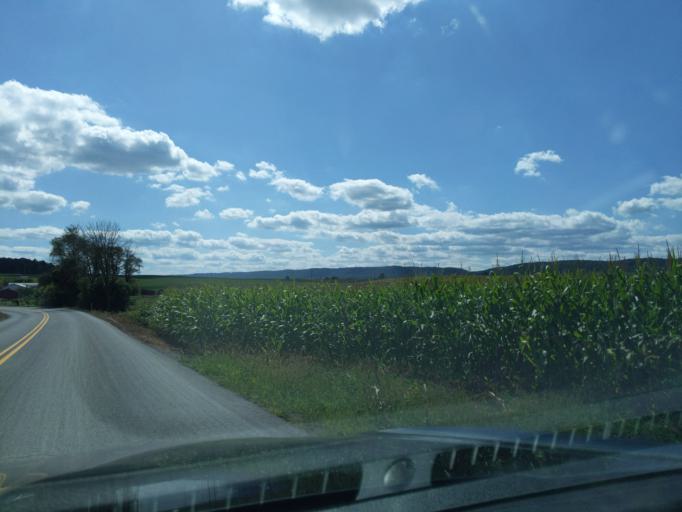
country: US
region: Pennsylvania
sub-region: Blair County
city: Tyrone
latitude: 40.6413
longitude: -78.2206
